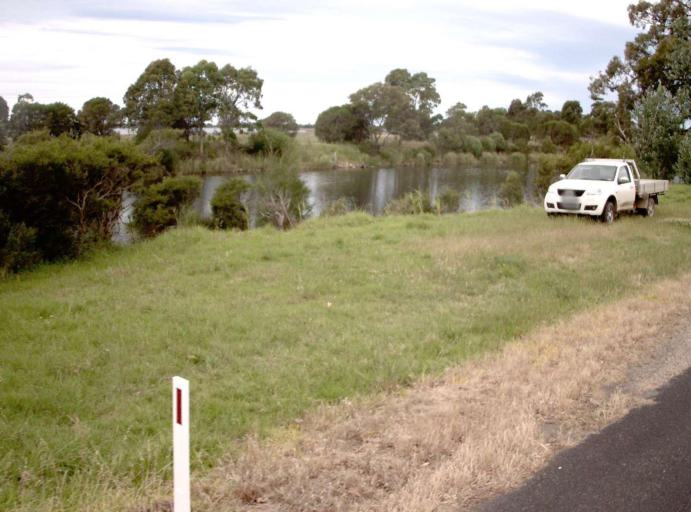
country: AU
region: Victoria
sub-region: East Gippsland
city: Bairnsdale
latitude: -37.8751
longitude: 147.6527
